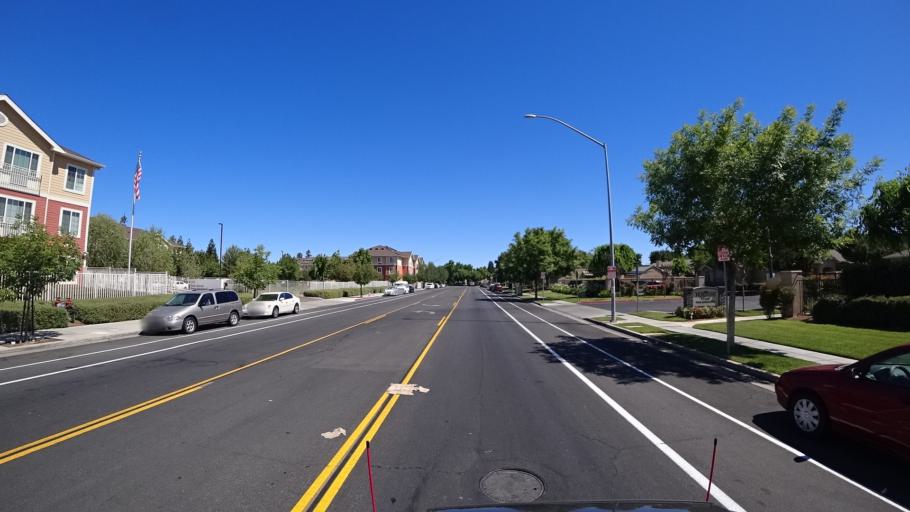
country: US
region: California
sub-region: Fresno County
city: West Park
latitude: 36.8101
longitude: -119.8581
